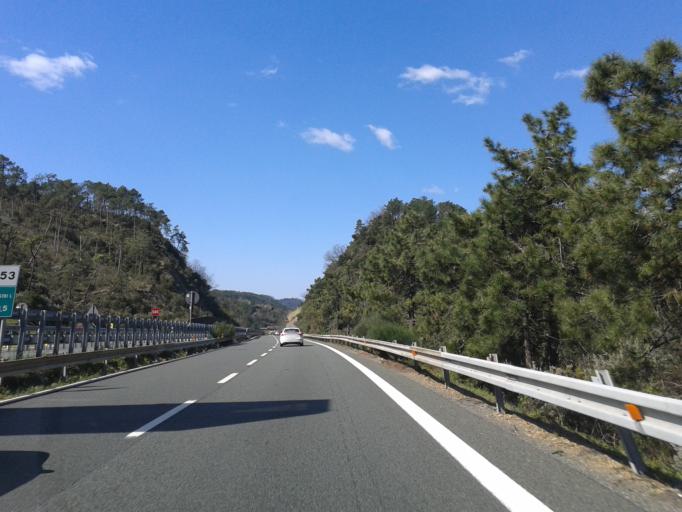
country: IT
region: Liguria
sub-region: Provincia di Genova
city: Casarza Ligure
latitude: 44.2712
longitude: 9.4671
